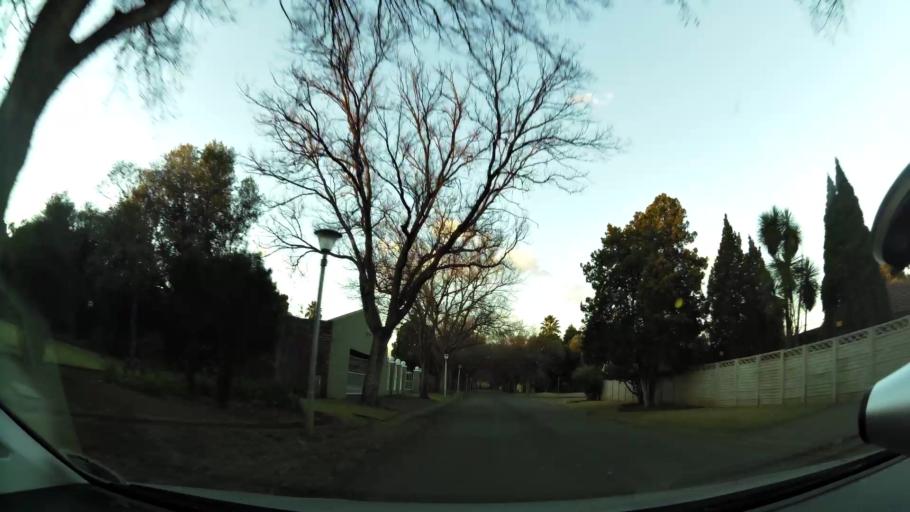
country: ZA
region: North-West
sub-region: Dr Kenneth Kaunda District Municipality
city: Potchefstroom
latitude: -26.7250
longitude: 27.1095
